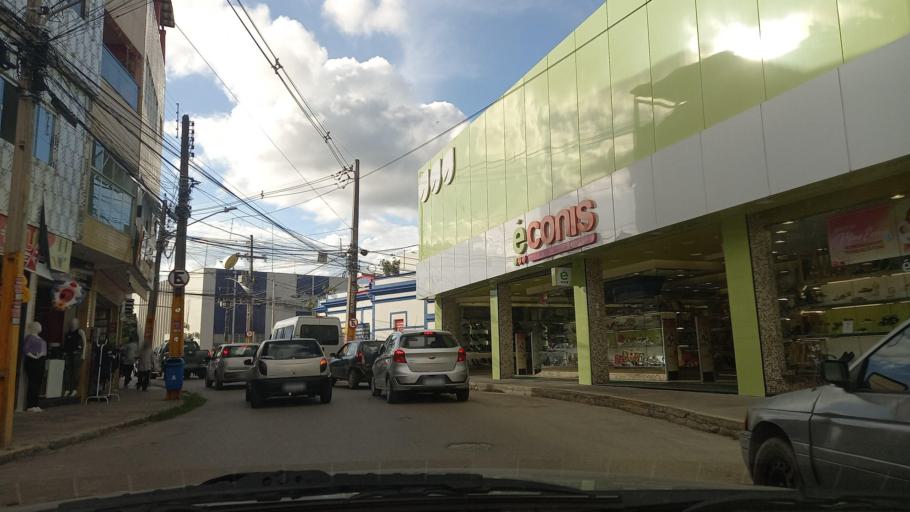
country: BR
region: Pernambuco
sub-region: Gravata
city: Gravata
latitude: -8.2032
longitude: -35.5670
